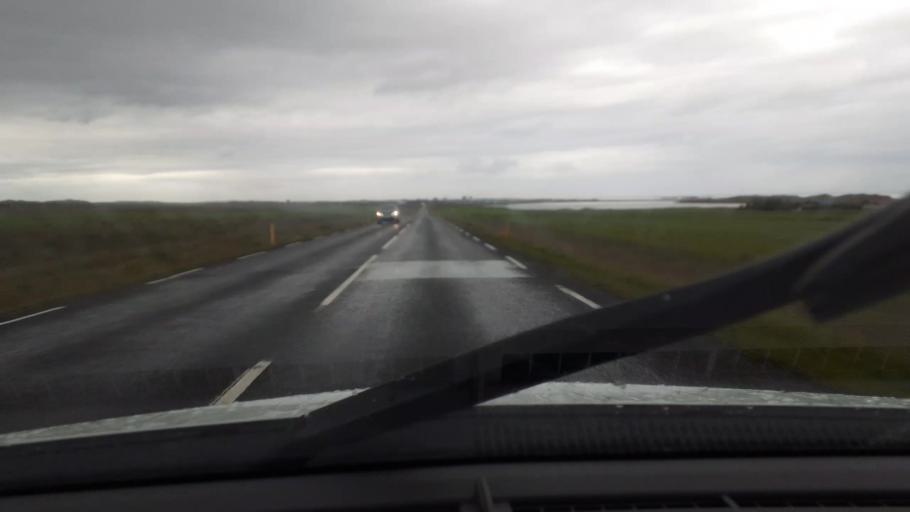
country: IS
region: West
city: Akranes
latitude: 64.3545
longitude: -21.9883
